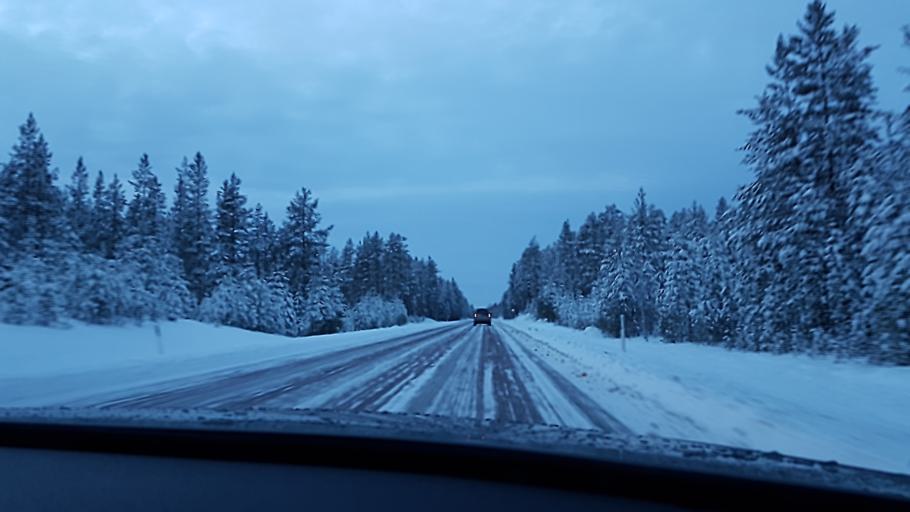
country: SE
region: Jaemtland
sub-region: Harjedalens Kommun
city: Sveg
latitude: 62.0462
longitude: 14.8066
